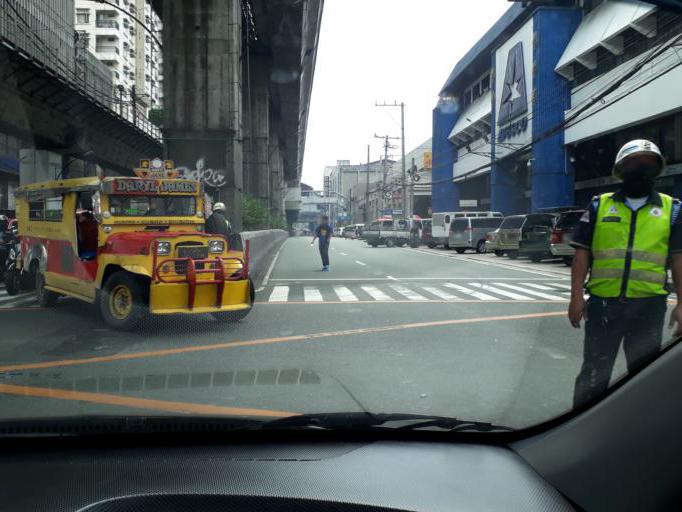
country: PH
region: Metro Manila
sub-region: Quezon City
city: Quezon City
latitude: 14.6243
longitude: 121.0555
